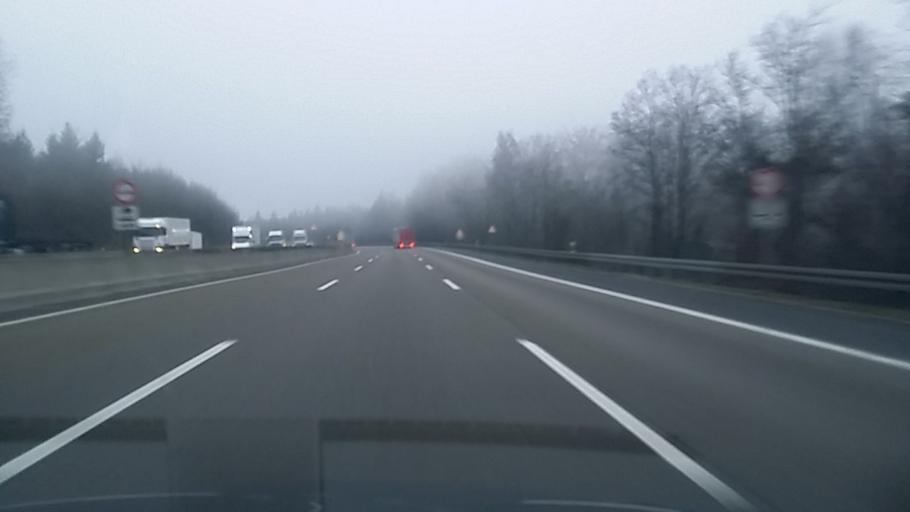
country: DE
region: Hesse
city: Schwarzenborn
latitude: 50.9562
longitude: 9.5017
